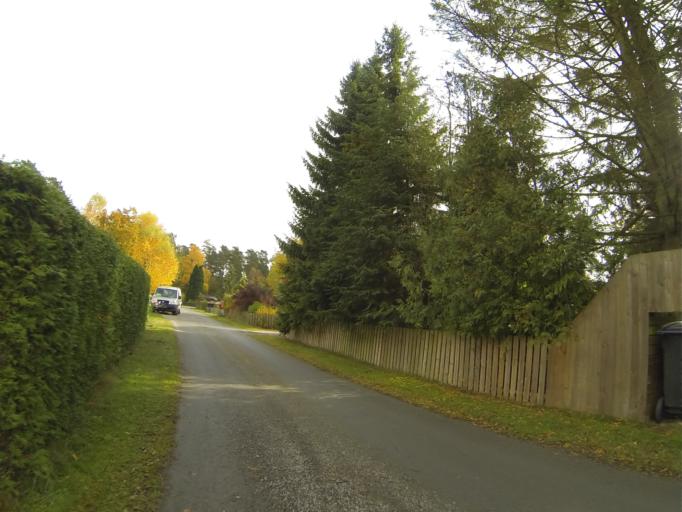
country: SE
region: Skane
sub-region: Sjobo Kommun
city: Sjoebo
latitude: 55.6343
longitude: 13.6446
